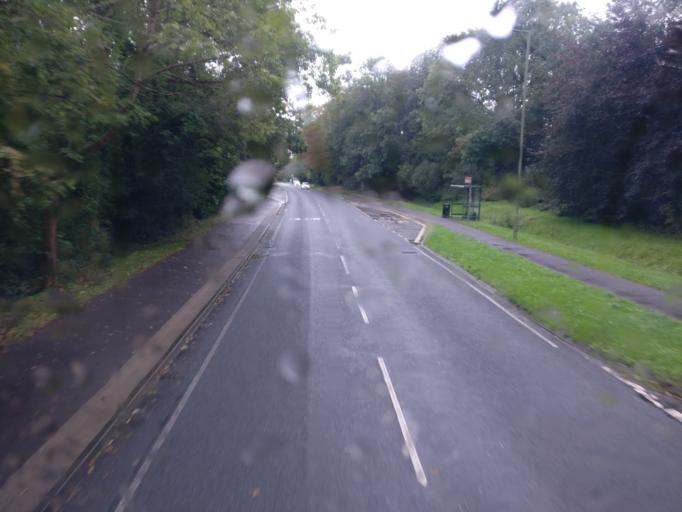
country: GB
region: England
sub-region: Hampshire
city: Basingstoke
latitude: 51.2523
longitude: -1.0838
